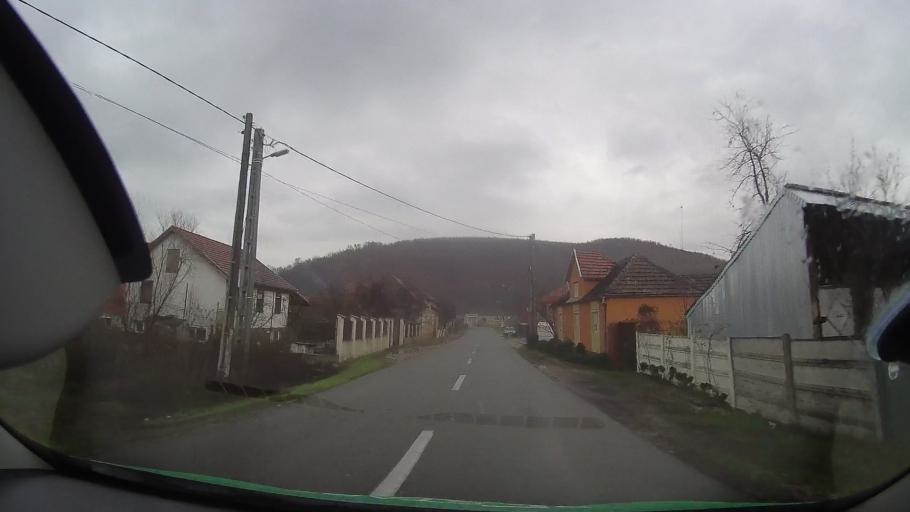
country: RO
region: Bihor
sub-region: Comuna Soimi
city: Soimi
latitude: 46.6829
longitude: 22.1160
